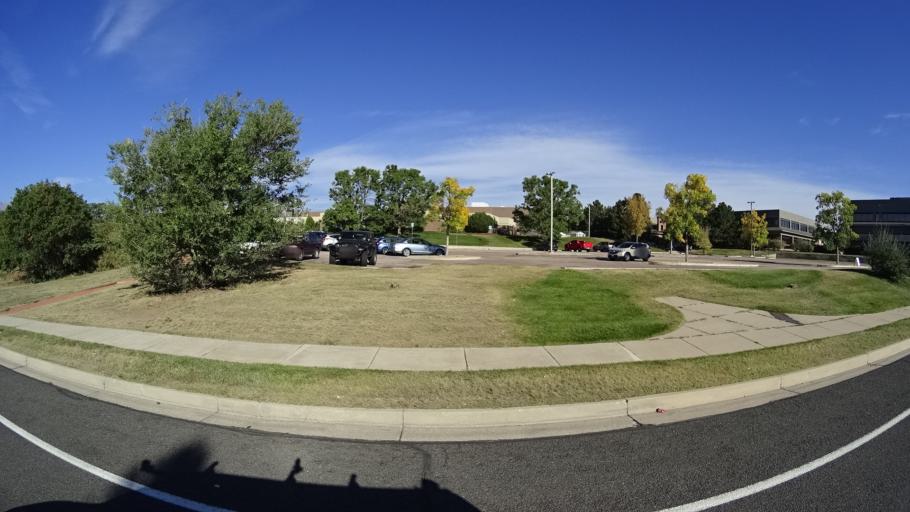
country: US
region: Colorado
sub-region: El Paso County
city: Colorado Springs
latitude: 38.9053
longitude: -104.7834
